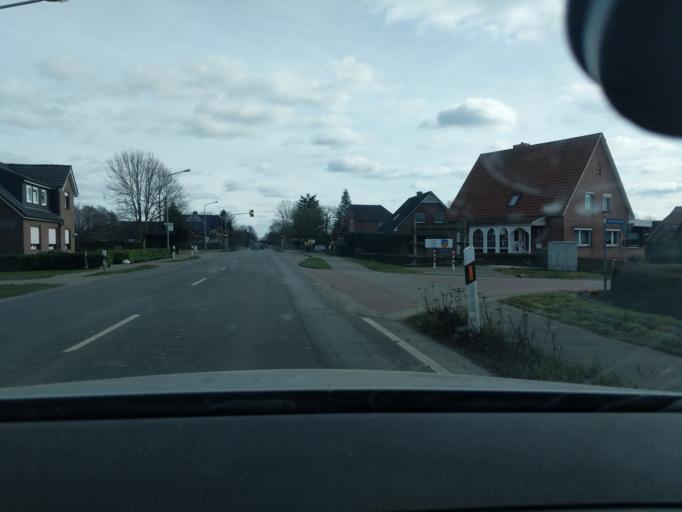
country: DE
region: Lower Saxony
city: Drochtersen
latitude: 53.7002
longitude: 9.4099
